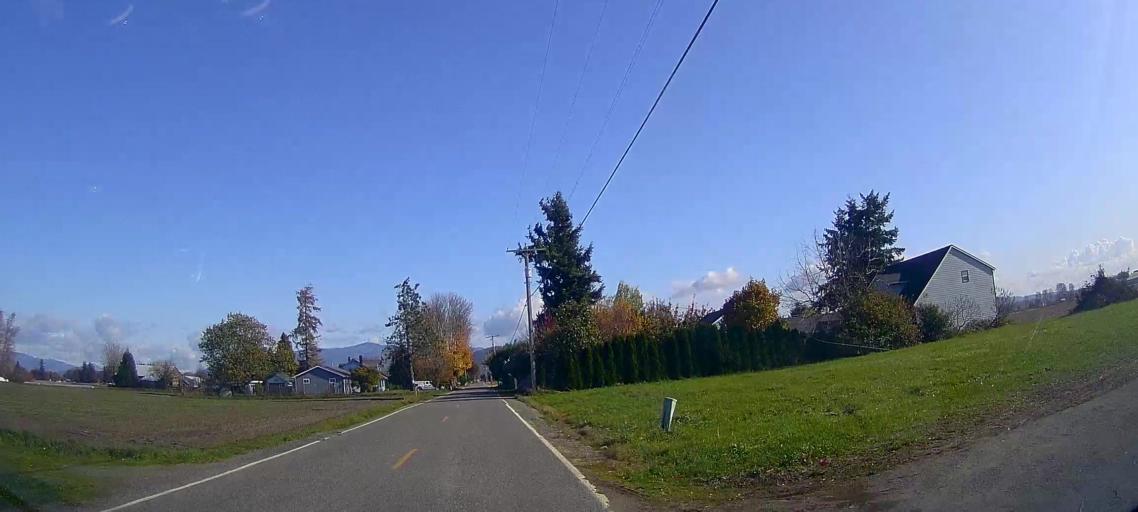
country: US
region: Washington
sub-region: Skagit County
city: Mount Vernon
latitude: 48.3992
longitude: -122.3942
